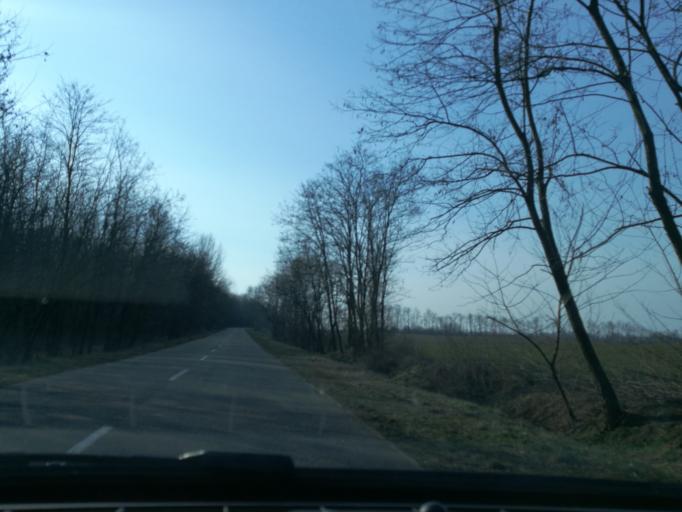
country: HU
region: Szabolcs-Szatmar-Bereg
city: Levelek
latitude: 47.9931
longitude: 21.9676
